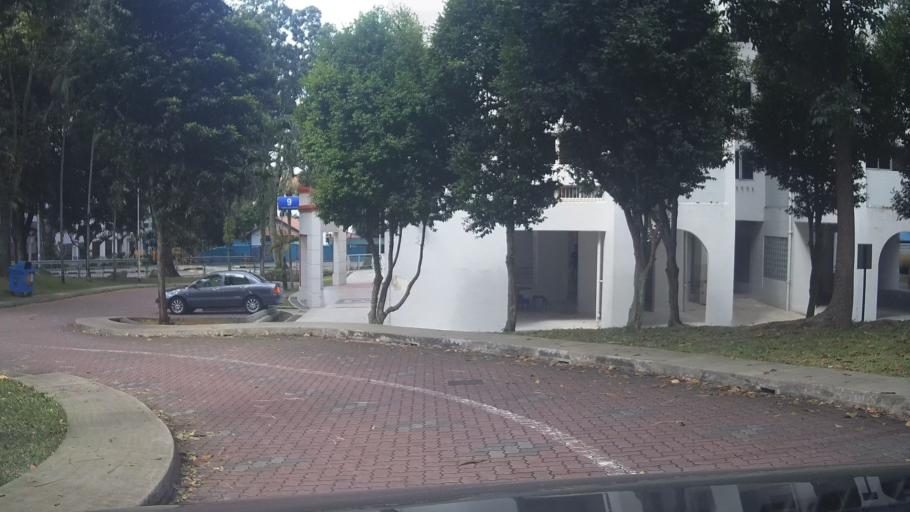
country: MY
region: Johor
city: Johor Bahru
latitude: 1.4409
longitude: 103.7765
